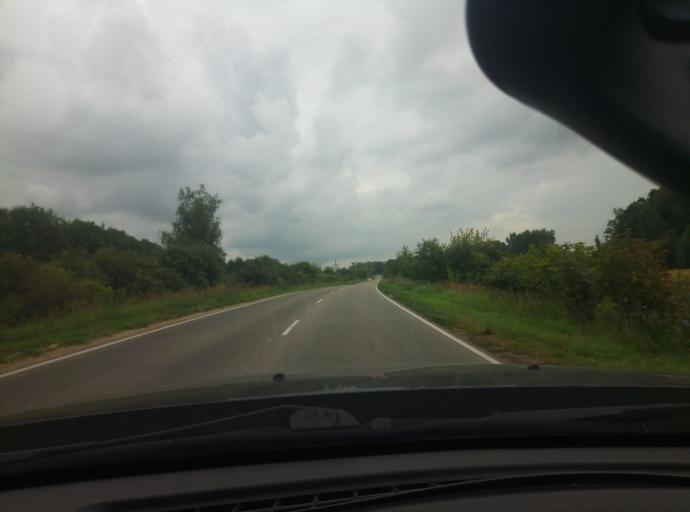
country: RU
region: Tula
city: Kimovsk
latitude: 53.9407
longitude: 38.5364
